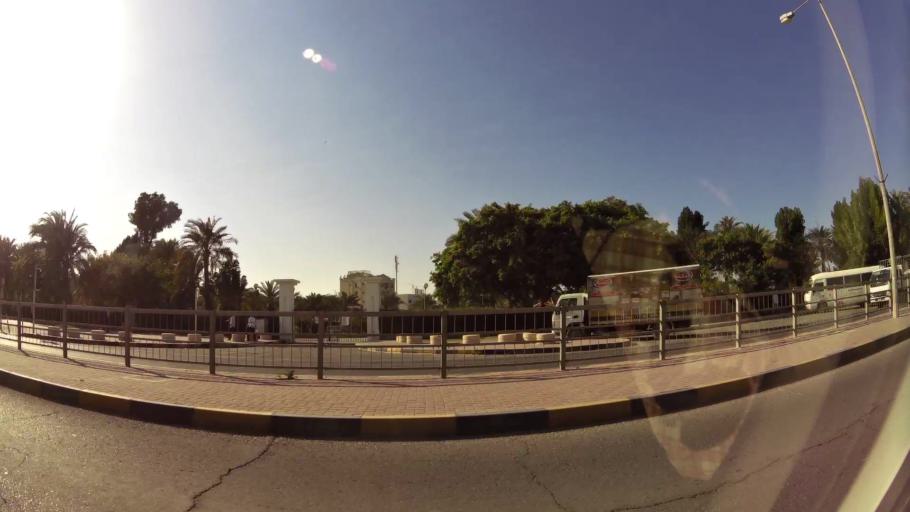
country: BH
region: Manama
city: Manama
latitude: 26.2207
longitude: 50.5686
